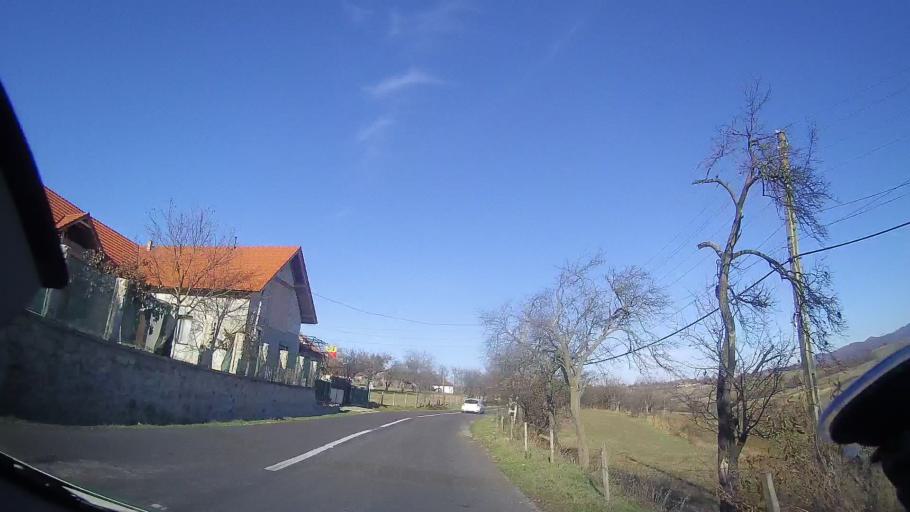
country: RO
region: Bihor
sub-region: Comuna Bratca
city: Beznea
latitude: 46.9651
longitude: 22.6160
